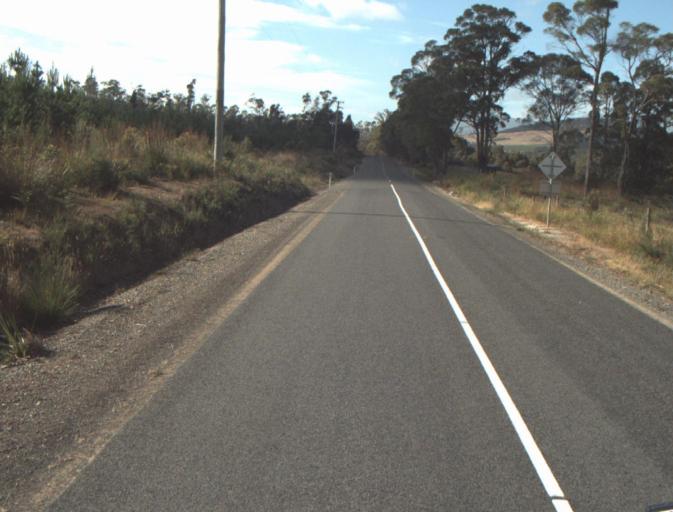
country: AU
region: Tasmania
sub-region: Dorset
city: Bridport
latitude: -41.1416
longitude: 147.2281
